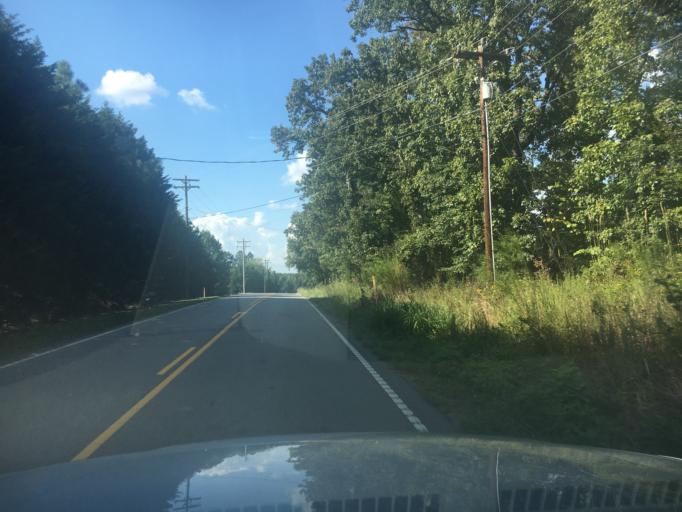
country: US
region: South Carolina
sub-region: Greenville County
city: Fountain Inn
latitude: 34.5989
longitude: -82.2285
